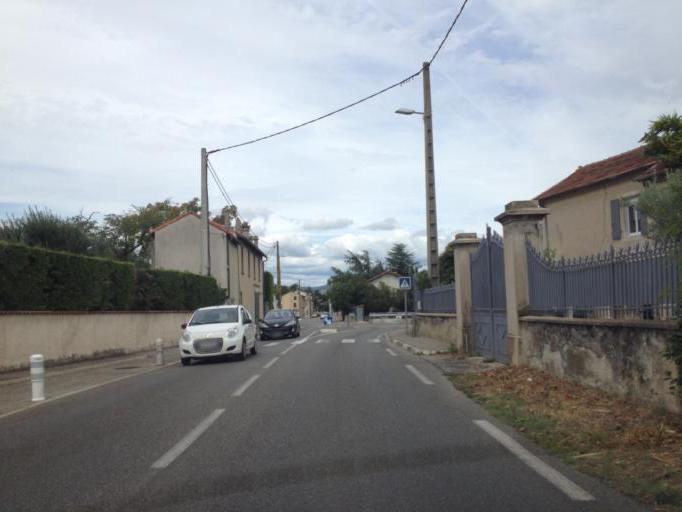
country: FR
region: Rhone-Alpes
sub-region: Departement de la Drome
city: Montelimar
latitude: 44.5470
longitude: 4.7543
